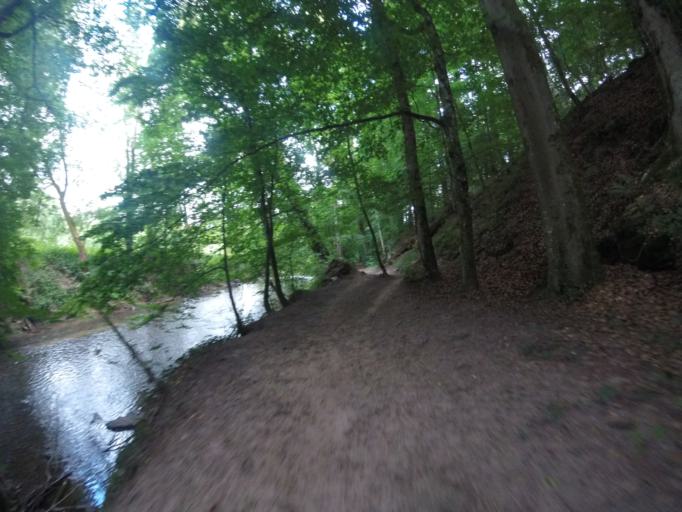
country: DE
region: Baden-Wuerttemberg
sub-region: Regierungsbezirk Stuttgart
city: Oppenweiler
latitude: 48.9593
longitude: 9.4631
